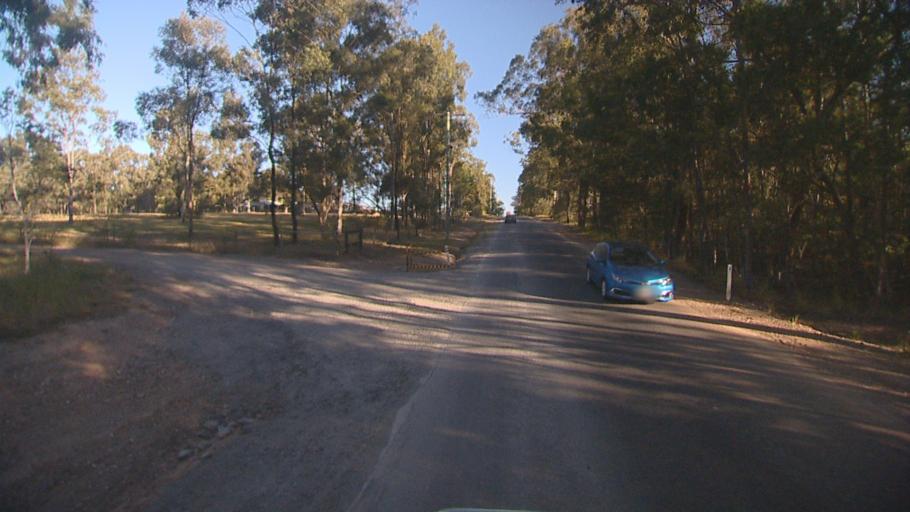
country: AU
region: Queensland
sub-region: Logan
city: Chambers Flat
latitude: -27.7759
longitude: 153.1364
